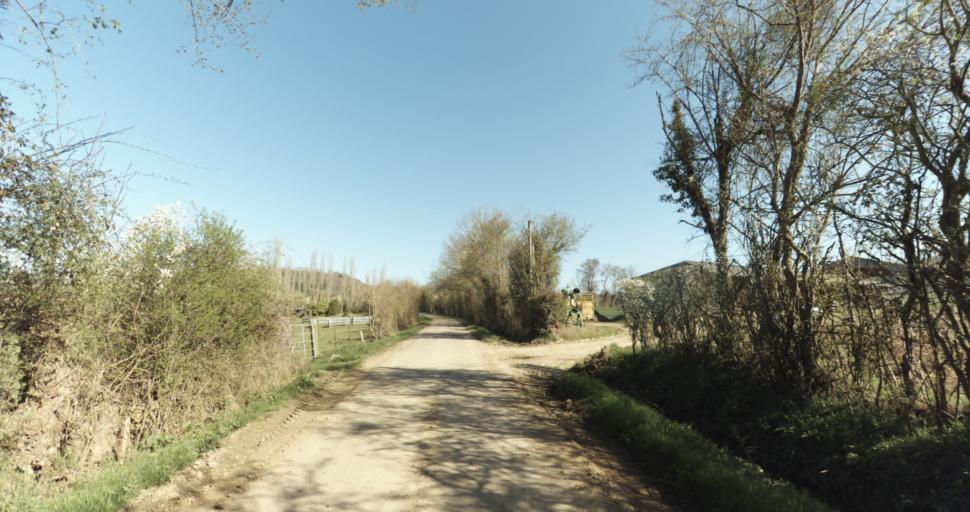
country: FR
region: Lower Normandy
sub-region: Departement du Calvados
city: Saint-Pierre-sur-Dives
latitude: 48.9703
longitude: 0.0524
